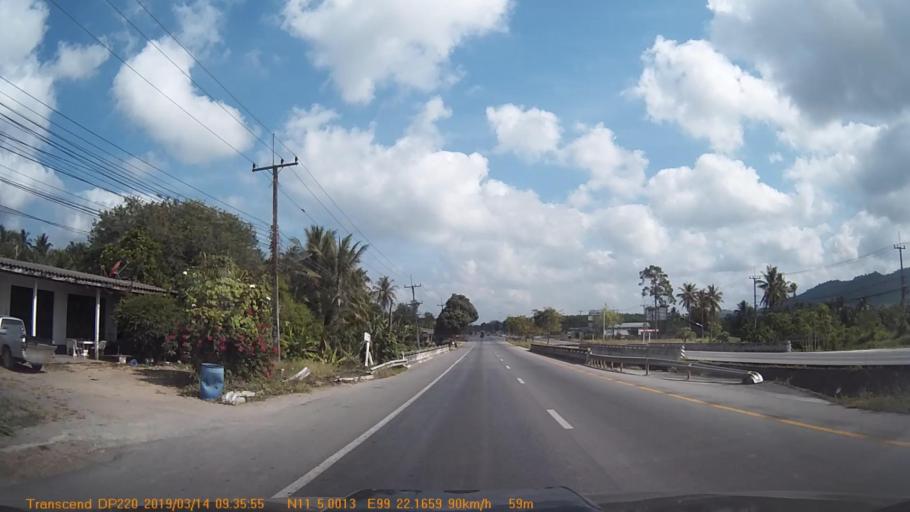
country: TH
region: Prachuap Khiri Khan
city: Bang Saphan Noi
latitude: 11.0843
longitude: 99.3695
